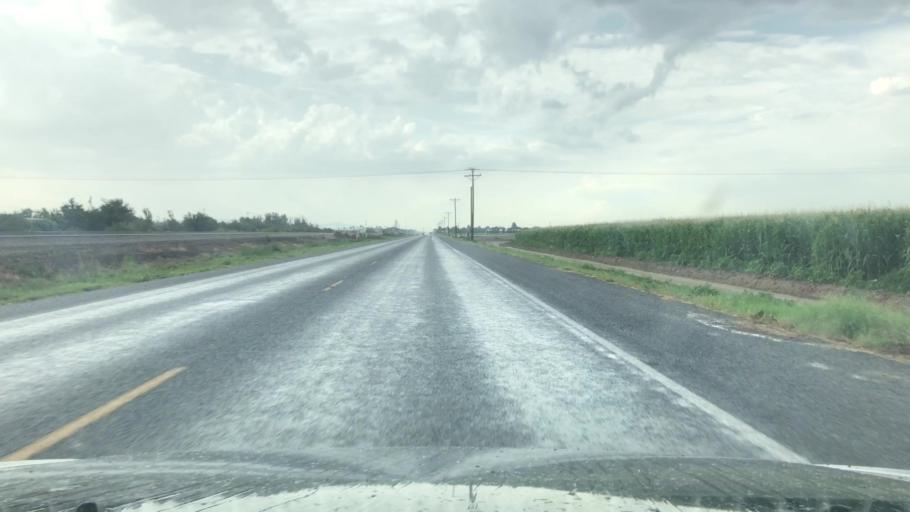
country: US
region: New Mexico
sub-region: Dona Ana County
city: Mesquite
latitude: 32.1520
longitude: -106.6886
